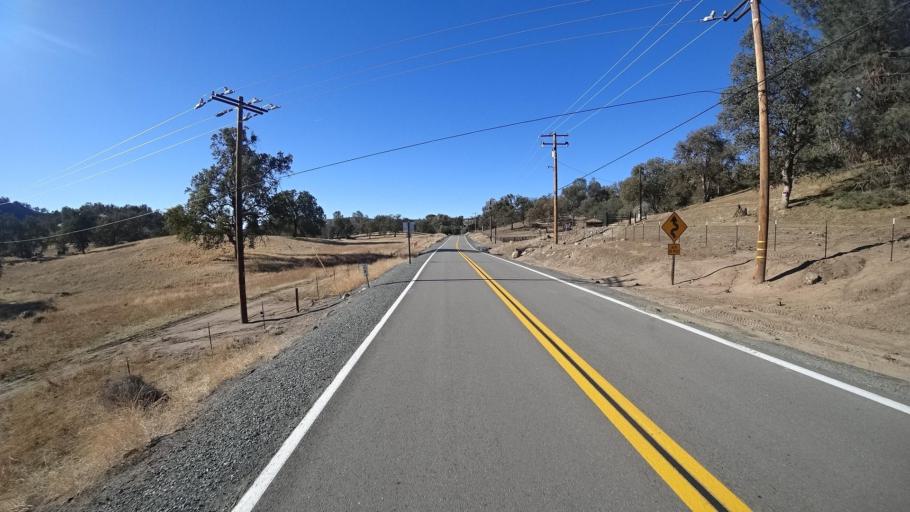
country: US
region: California
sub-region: Kern County
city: Alta Sierra
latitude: 35.7141
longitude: -118.7290
